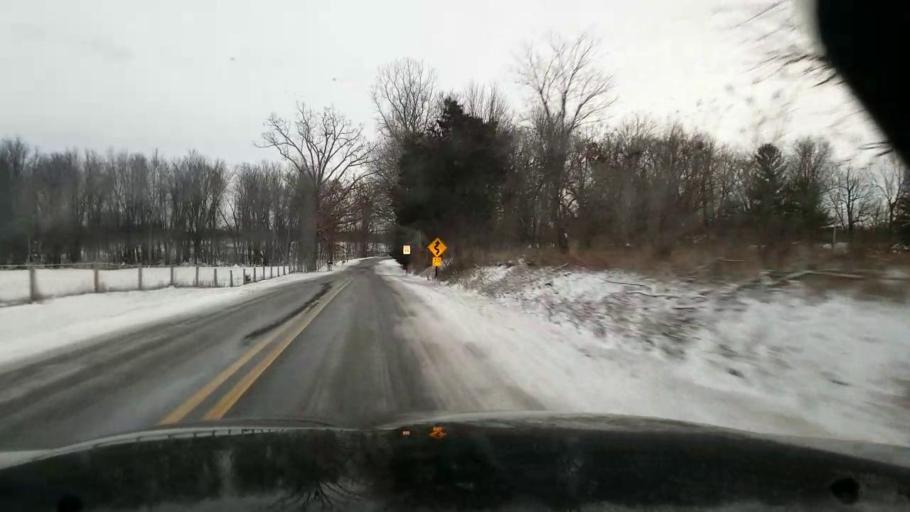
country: US
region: Michigan
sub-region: Jackson County
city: Vandercook Lake
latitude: 42.0895
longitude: -84.4658
